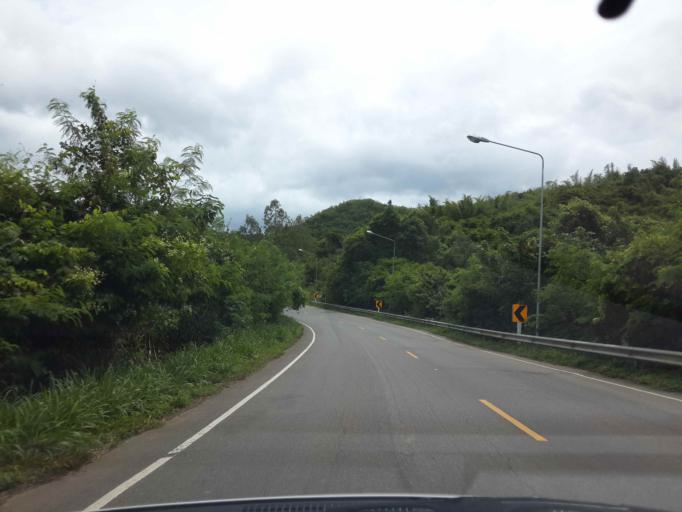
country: TH
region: Ratchaburi
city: Suan Phueng
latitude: 13.5473
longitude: 99.2795
